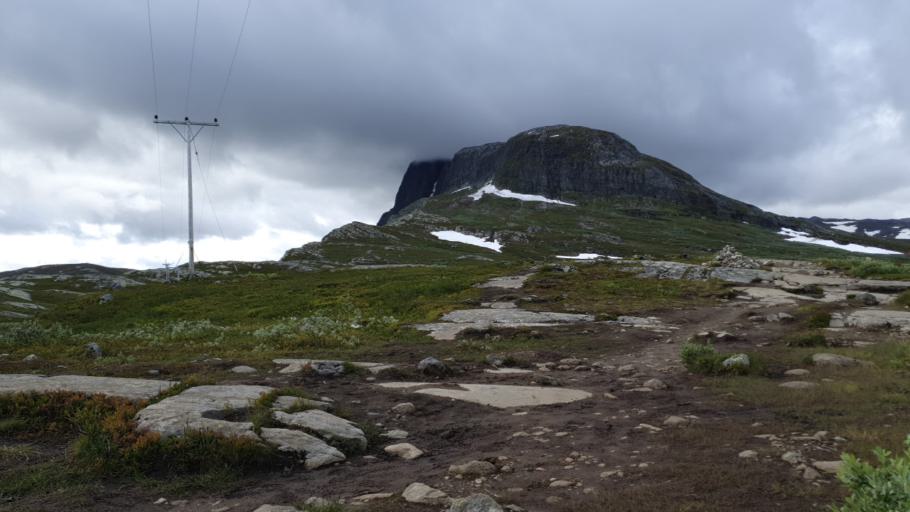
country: NO
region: Oppland
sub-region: Vestre Slidre
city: Slidre
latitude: 61.3173
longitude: 8.8036
